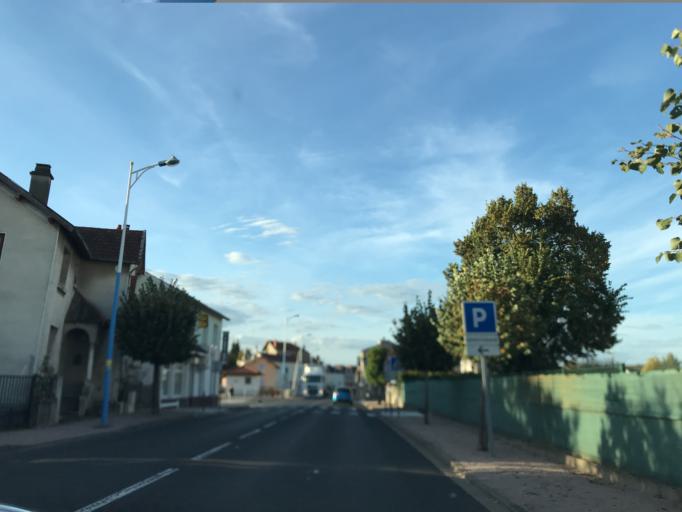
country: FR
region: Auvergne
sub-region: Departement du Puy-de-Dome
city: Puy-Guillaume
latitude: 45.9575
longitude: 3.4757
